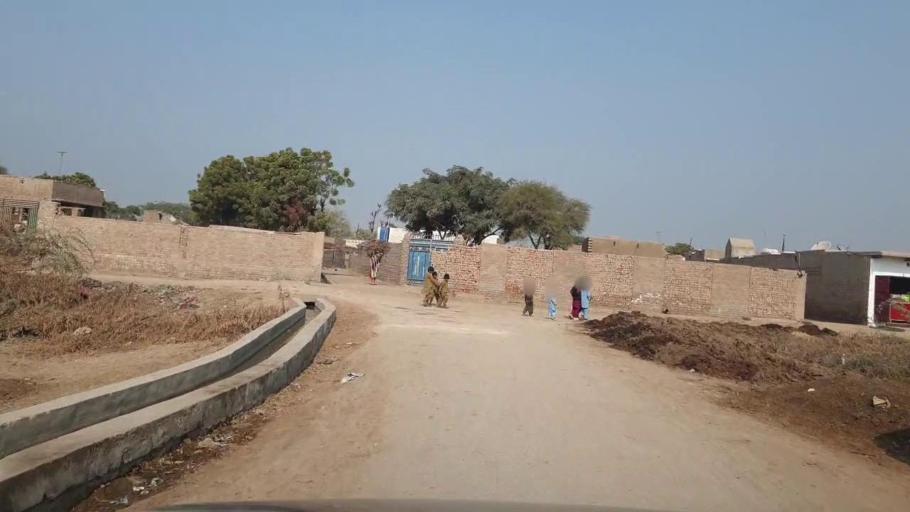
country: PK
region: Sindh
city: Bhit Shah
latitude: 25.7988
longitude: 68.4924
